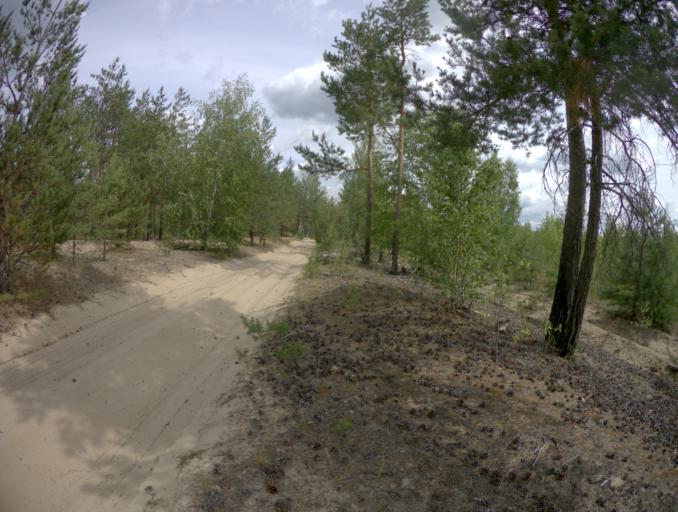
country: RU
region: Nizjnij Novgorod
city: Frolishchi
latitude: 56.4974
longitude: 42.5511
